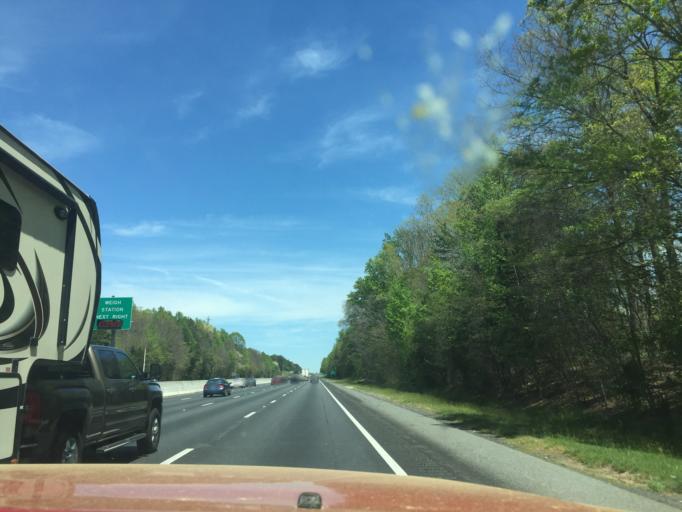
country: US
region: North Carolina
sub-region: Mecklenburg County
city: Pineville
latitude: 35.0716
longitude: -80.9483
